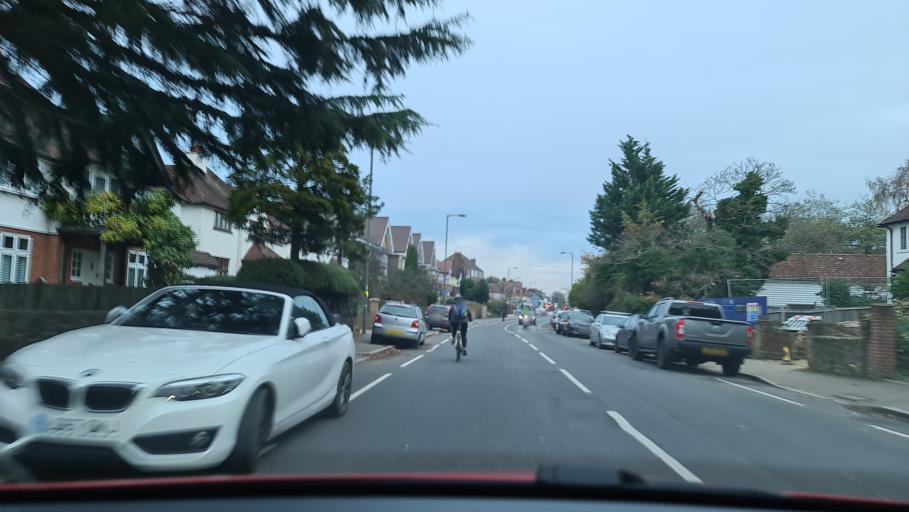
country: GB
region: England
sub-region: Surrey
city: Thames Ditton
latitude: 51.3879
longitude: -0.3282
